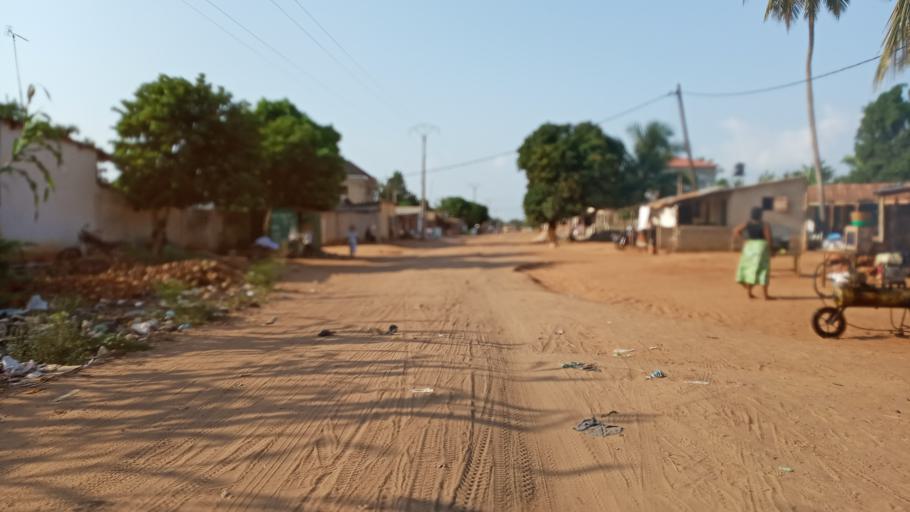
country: TG
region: Maritime
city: Lome
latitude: 6.1756
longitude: 1.1520
